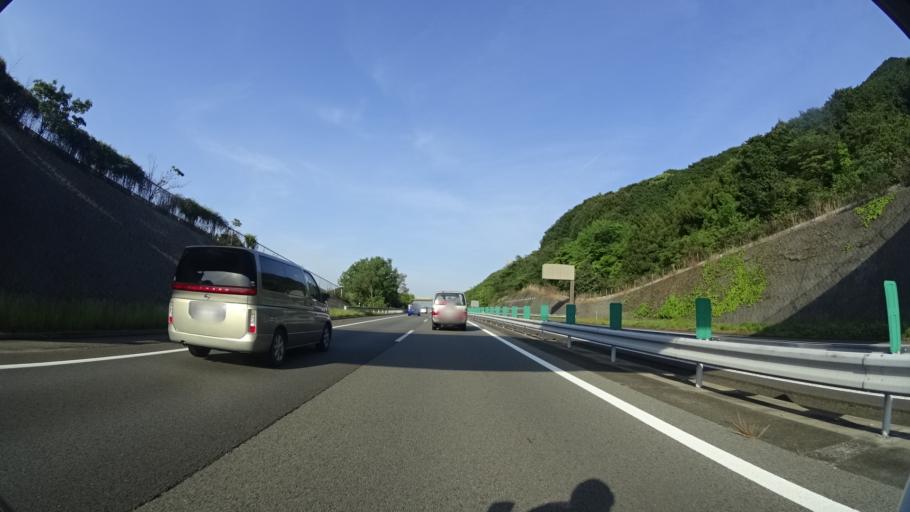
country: JP
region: Ehime
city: Kawanoecho
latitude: 33.9562
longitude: 133.4713
